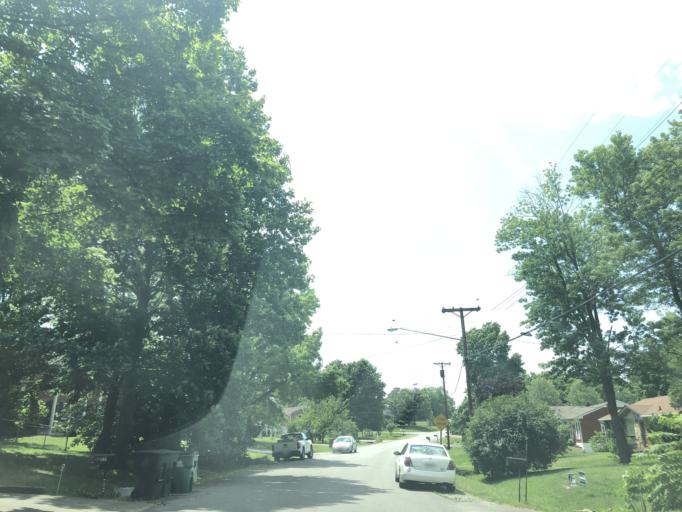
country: US
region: Tennessee
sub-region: Davidson County
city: Oak Hill
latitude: 36.0815
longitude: -86.7494
